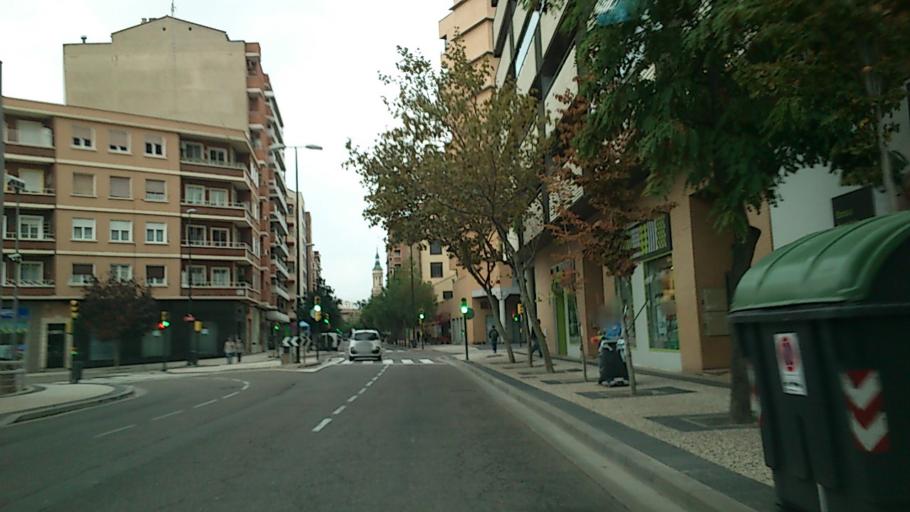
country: ES
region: Aragon
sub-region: Provincia de Zaragoza
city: Zaragoza
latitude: 41.6605
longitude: -0.8689
